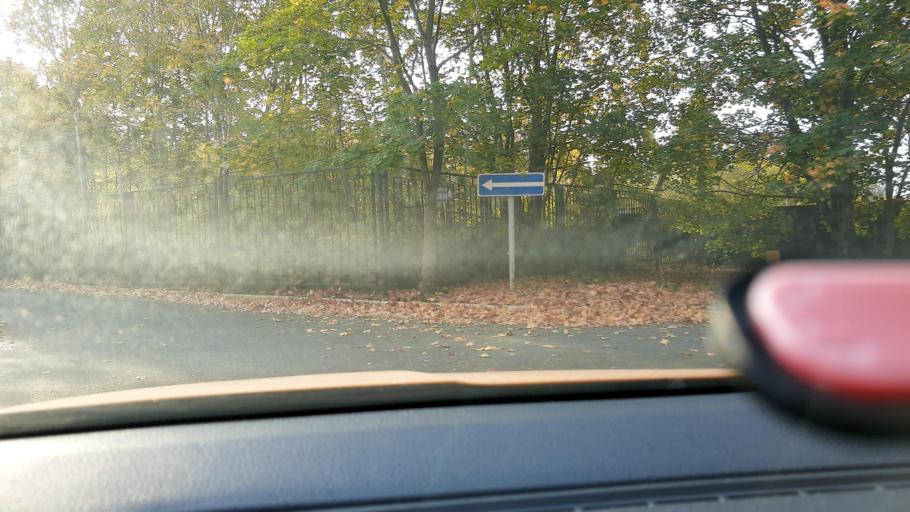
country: RU
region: Moskovskaya
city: Lesnoy Gorodok
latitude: 55.6473
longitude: 37.2423
